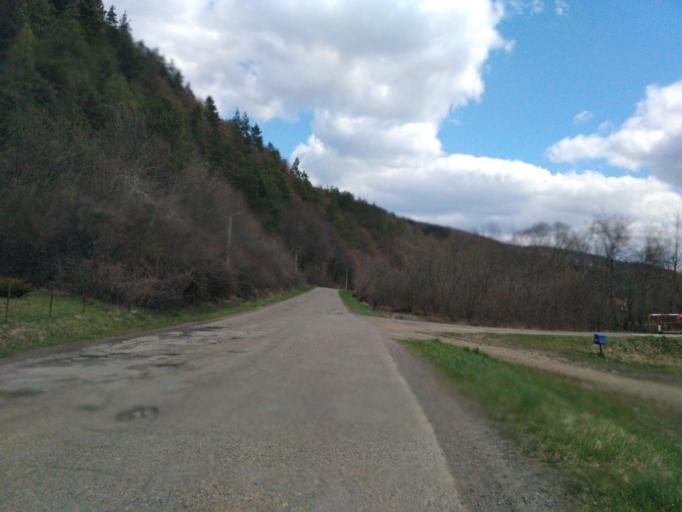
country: PL
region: Subcarpathian Voivodeship
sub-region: Powiat sanocki
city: Tyrawa Woloska
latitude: 49.6076
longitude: 22.2880
